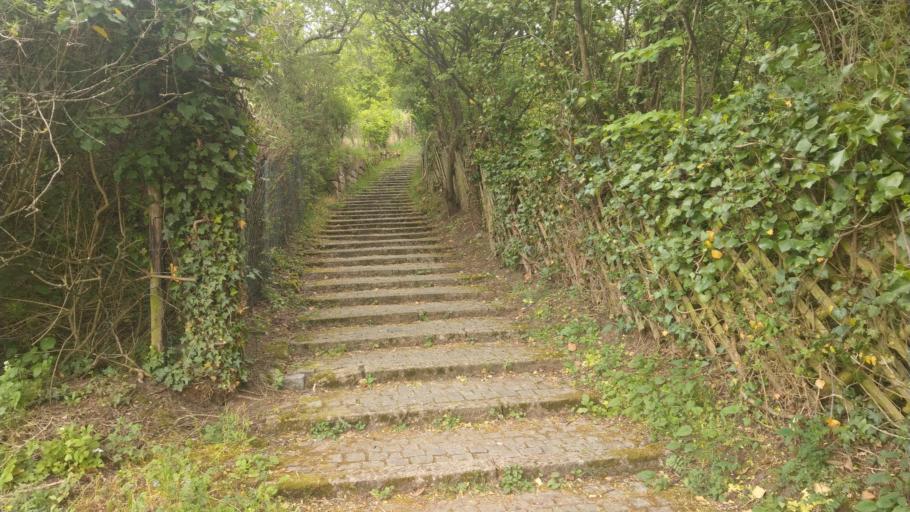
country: DE
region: Baden-Wuerttemberg
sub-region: Regierungsbezirk Stuttgart
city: Esslingen
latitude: 48.7637
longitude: 9.2757
